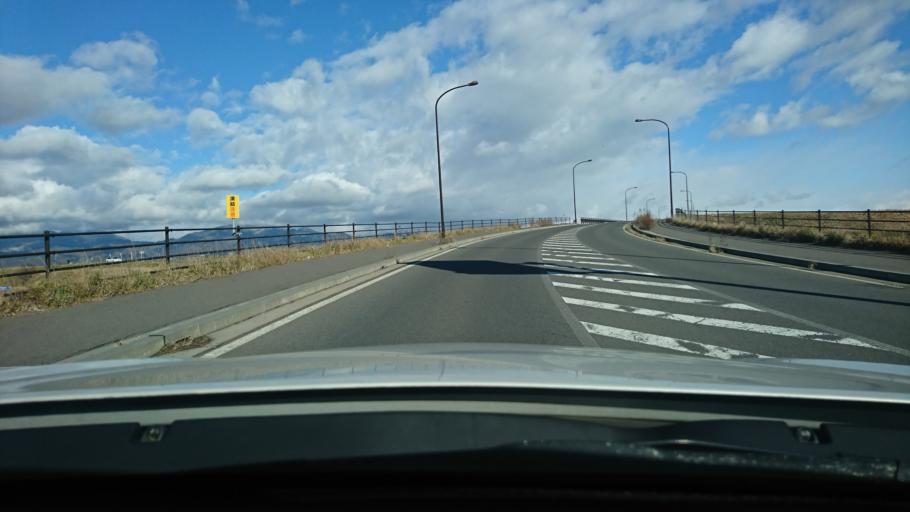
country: JP
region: Nagano
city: Nagano-shi
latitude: 36.5646
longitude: 138.1729
